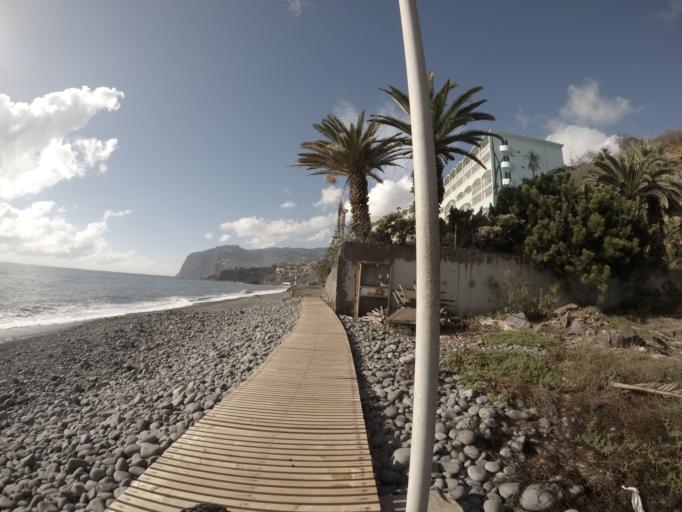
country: PT
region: Madeira
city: Camara de Lobos
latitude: 32.6375
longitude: -16.9483
